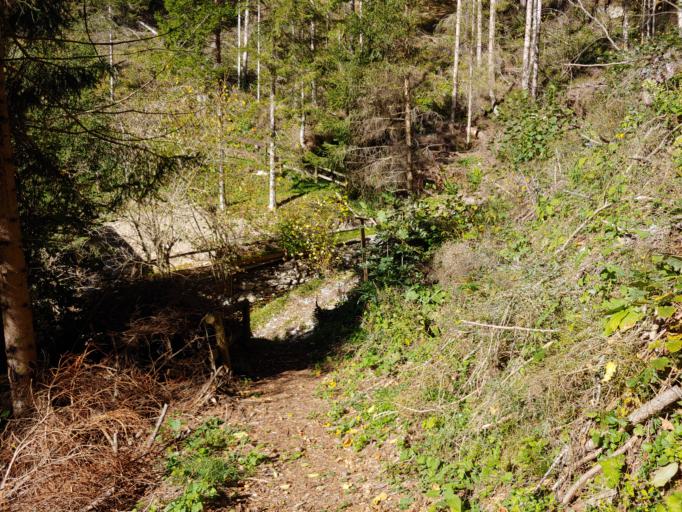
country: IT
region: Veneto
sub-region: Provincia di Belluno
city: Lozzo di Cadore
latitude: 46.4906
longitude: 12.4383
